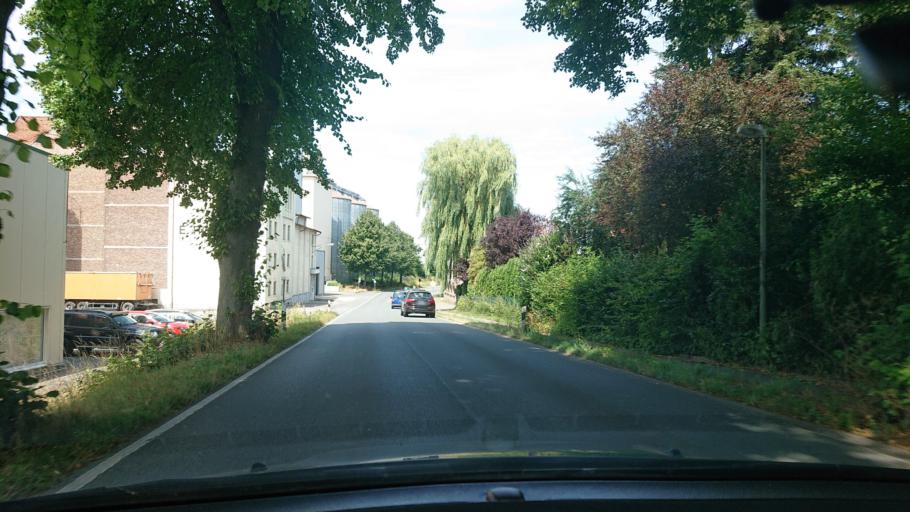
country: DE
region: North Rhine-Westphalia
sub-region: Regierungsbezirk Arnsberg
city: Mohnesee
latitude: 51.5170
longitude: 8.0902
